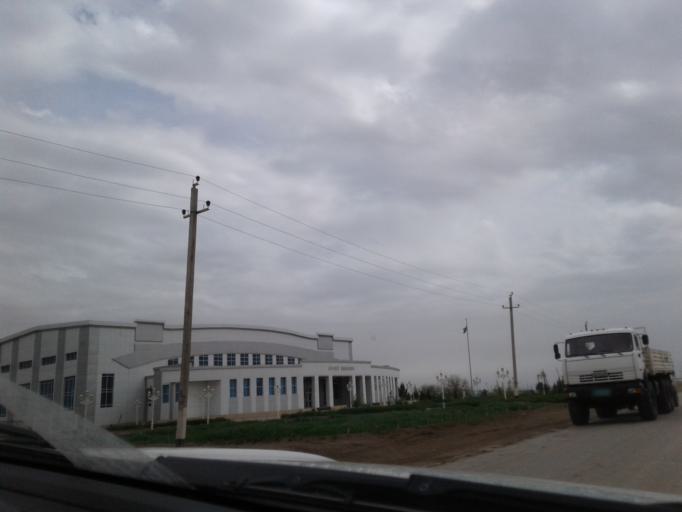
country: TM
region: Lebap
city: Atamyrat
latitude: 38.2203
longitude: 64.7257
